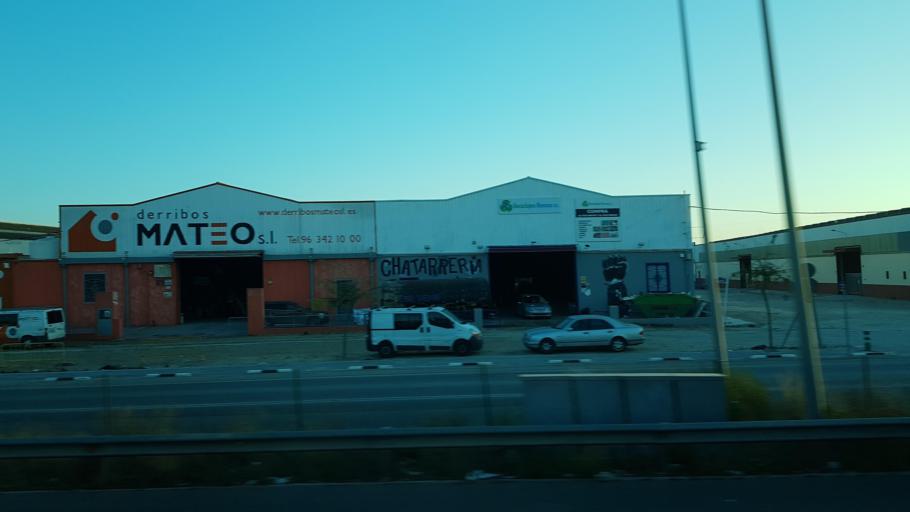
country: ES
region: Valencia
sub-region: Provincia de Valencia
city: Manises
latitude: 39.4794
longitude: -0.4689
